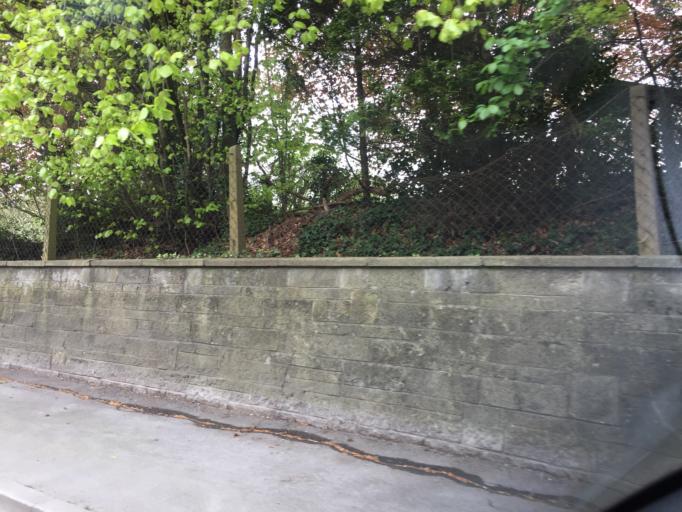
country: GB
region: England
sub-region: Bath and North East Somerset
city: Midsomer Norton
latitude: 51.2820
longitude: -2.4821
